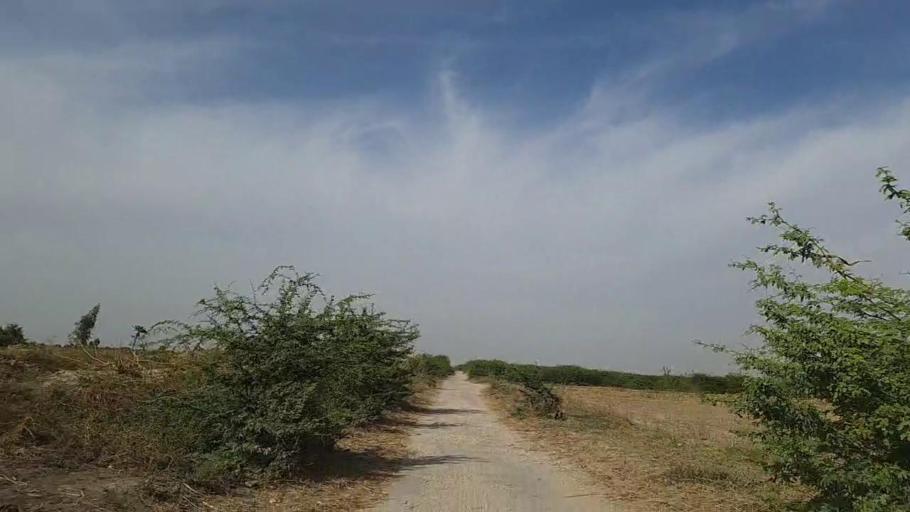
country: PK
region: Sindh
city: Samaro
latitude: 25.2414
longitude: 69.4237
